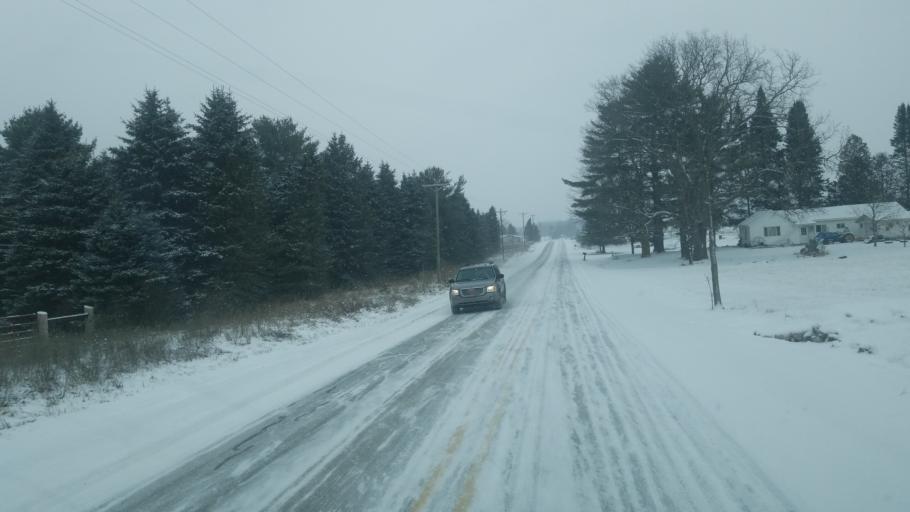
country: US
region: Michigan
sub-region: Osceola County
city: Reed City
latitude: 43.8149
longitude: -85.4041
